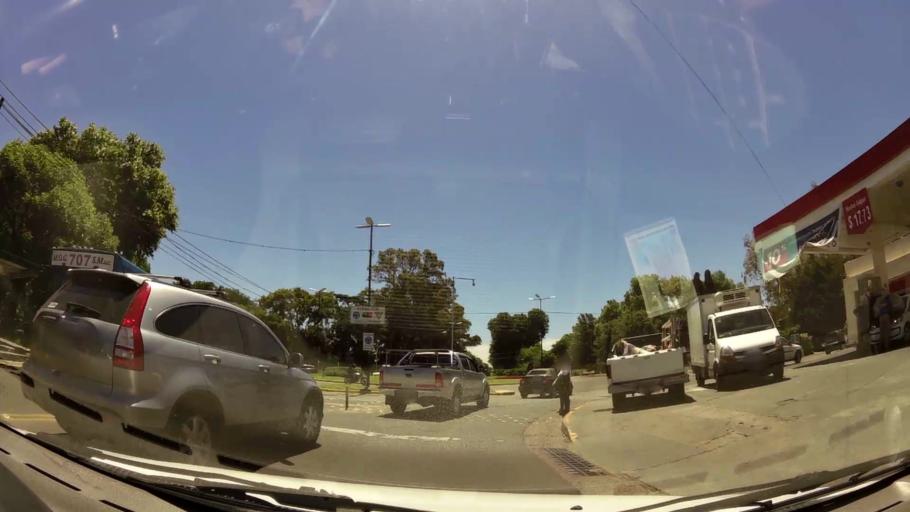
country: AR
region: Buenos Aires
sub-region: Partido de San Isidro
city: San Isidro
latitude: -34.4899
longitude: -58.5245
